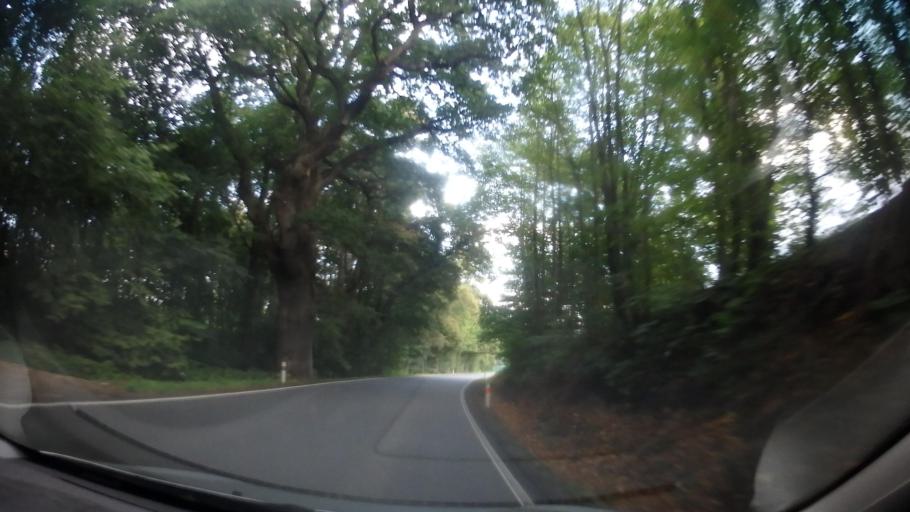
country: CZ
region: Olomoucky
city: Zabreh
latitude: 49.8869
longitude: 16.8476
